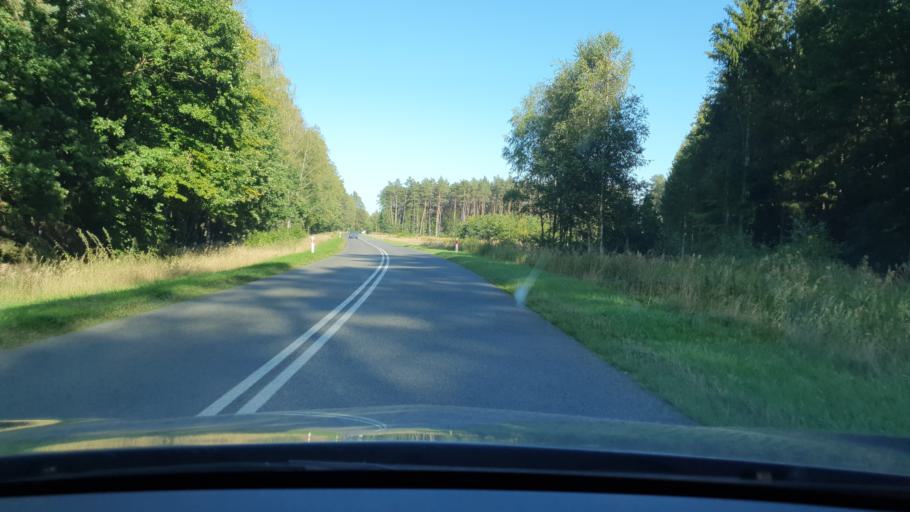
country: PL
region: West Pomeranian Voivodeship
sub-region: Powiat goleniowski
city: Przybiernow
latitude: 53.8229
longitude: 14.8223
